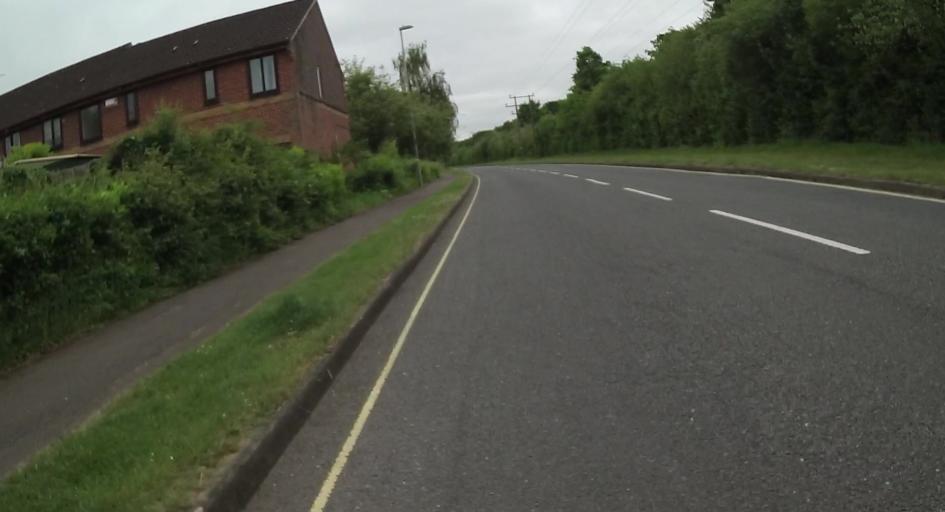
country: GB
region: England
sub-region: Hampshire
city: Basingstoke
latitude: 51.2928
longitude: -1.0645
